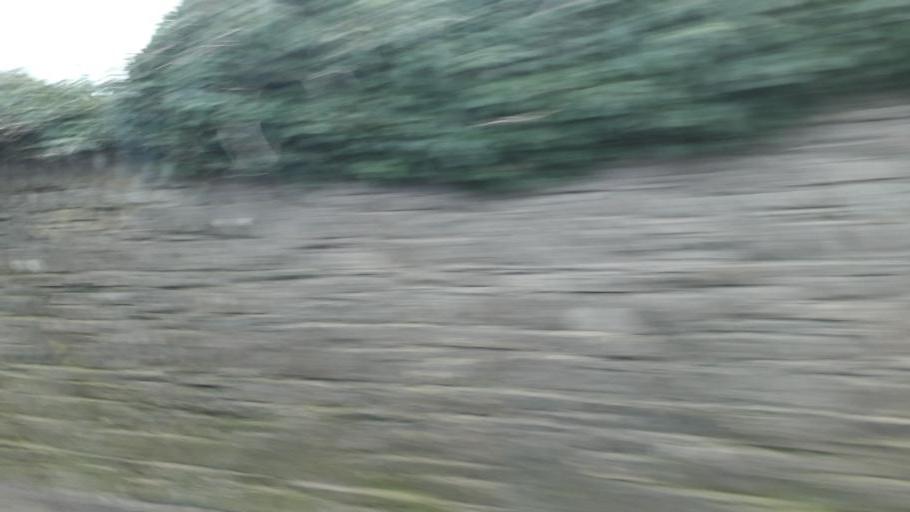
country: IE
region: Leinster
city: An Ros
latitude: 53.5317
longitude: -6.0915
